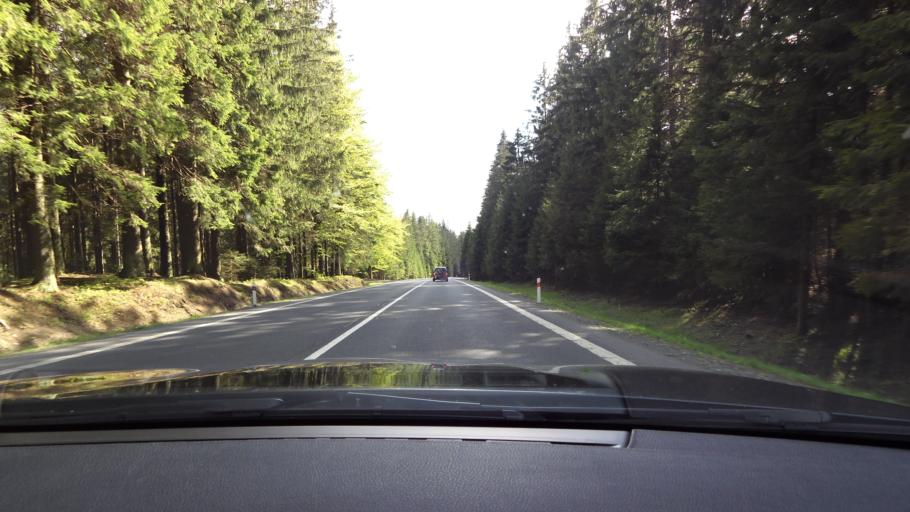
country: CZ
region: Plzensky
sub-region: Okres Klatovy
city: Zelezna Ruda
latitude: 49.1818
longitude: 13.2991
